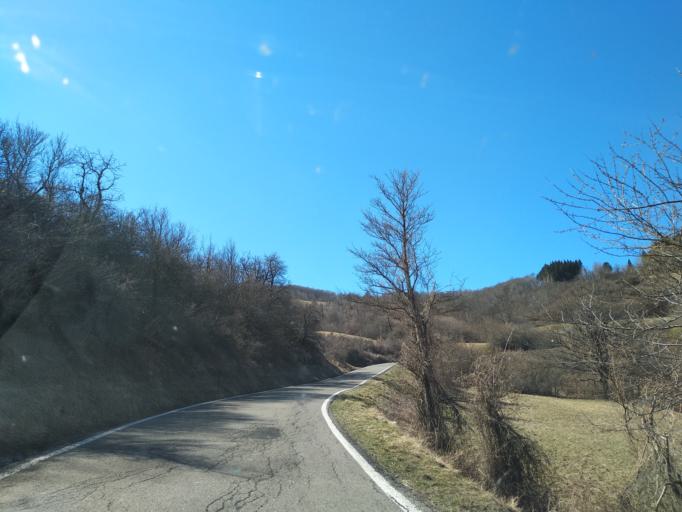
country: IT
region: Emilia-Romagna
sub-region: Provincia di Reggio Emilia
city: Ramiseto
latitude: 44.4048
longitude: 10.2673
